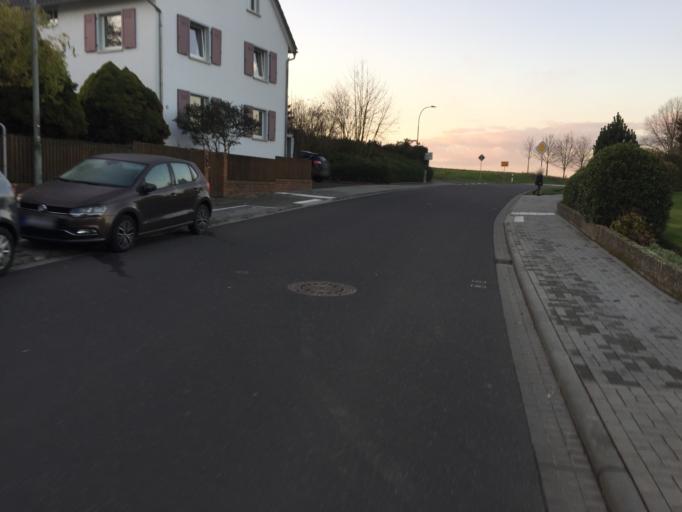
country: DE
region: Hesse
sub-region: Regierungsbezirk Giessen
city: Langgons
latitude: 50.5123
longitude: 8.7279
